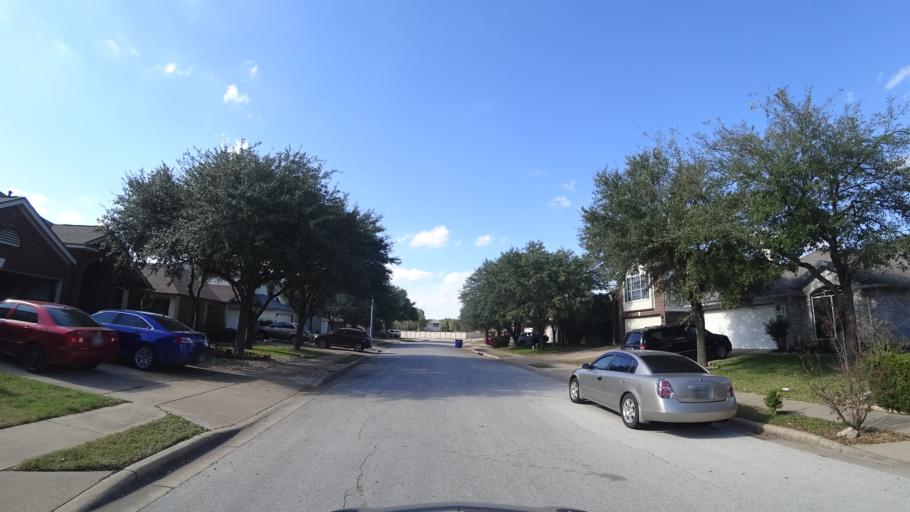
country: US
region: Texas
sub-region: Travis County
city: Wells Branch
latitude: 30.4579
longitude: -97.6815
